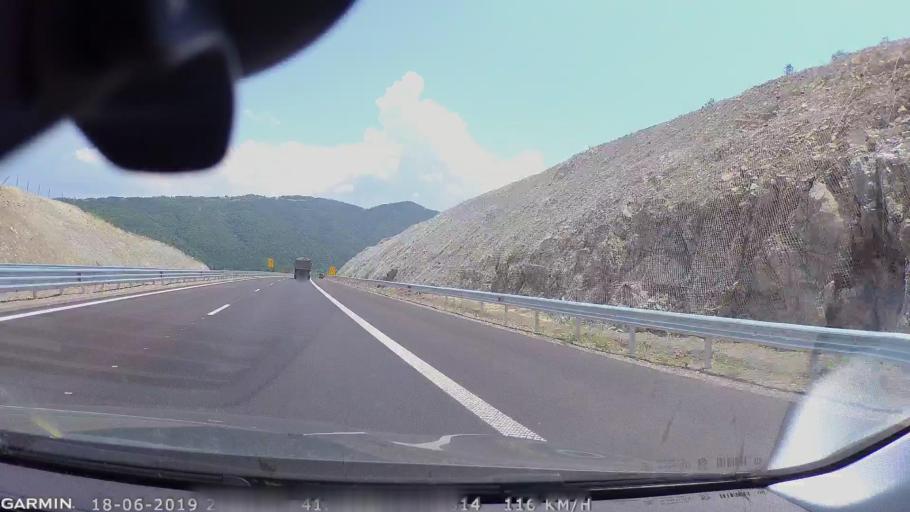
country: BG
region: Blagoevgrad
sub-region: Obshtina Blagoevgrad
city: Blagoevgrad
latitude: 41.9683
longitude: 23.0895
